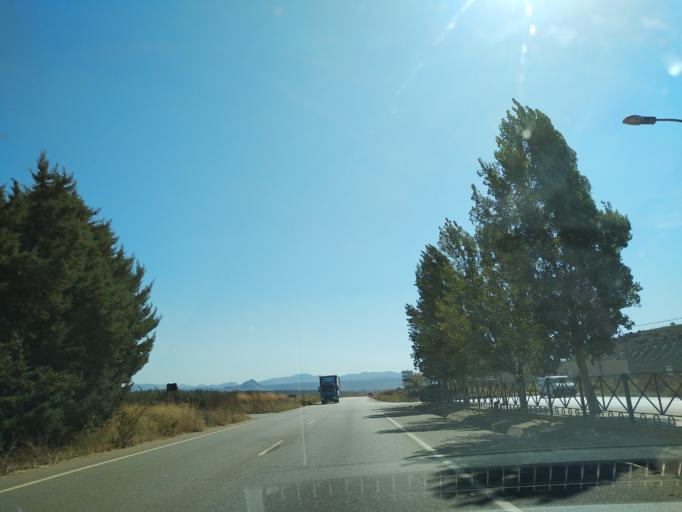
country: ES
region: Andalusia
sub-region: Provincia de Malaga
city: Mollina
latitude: 37.1160
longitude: -4.6521
